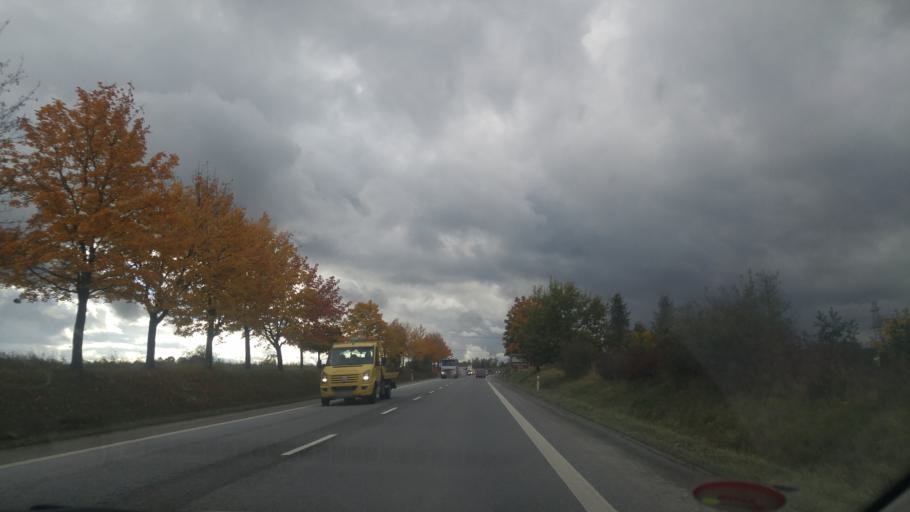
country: CZ
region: Jihocesky
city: Sevetin
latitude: 49.1167
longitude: 14.5873
